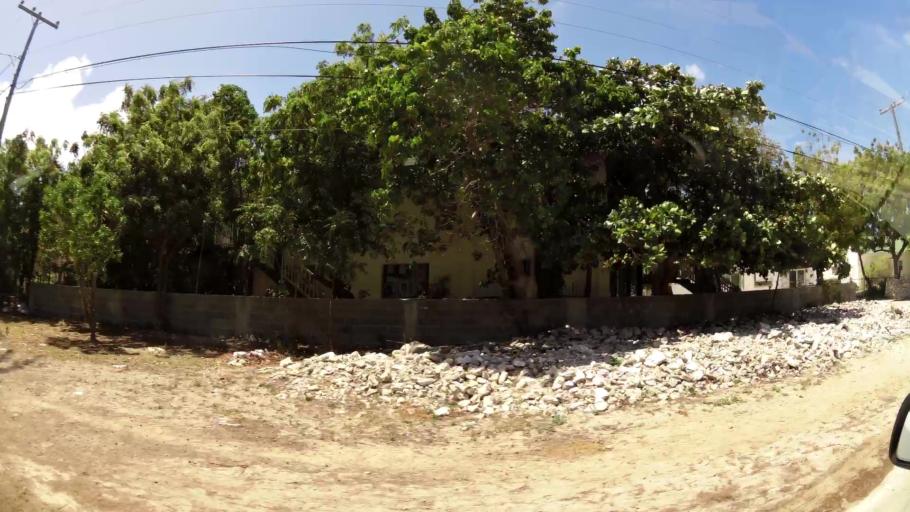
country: TC
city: Cockburn Town
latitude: 21.4500
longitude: -71.1435
